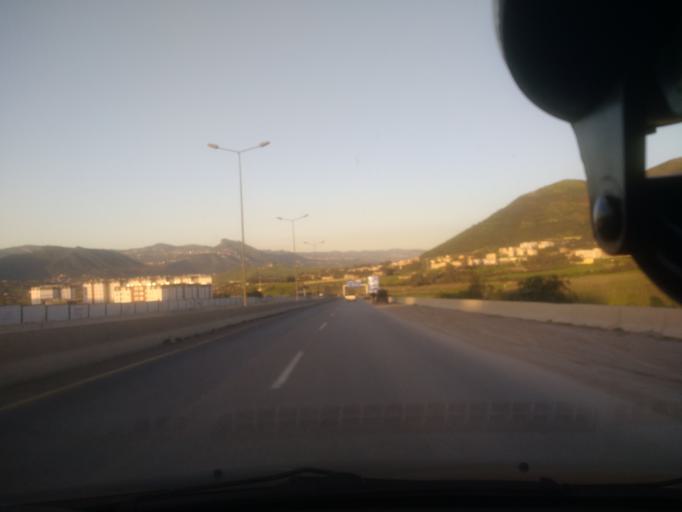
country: DZ
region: Boumerdes
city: Draa Ben Khedda
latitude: 36.7365
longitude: 4.0019
